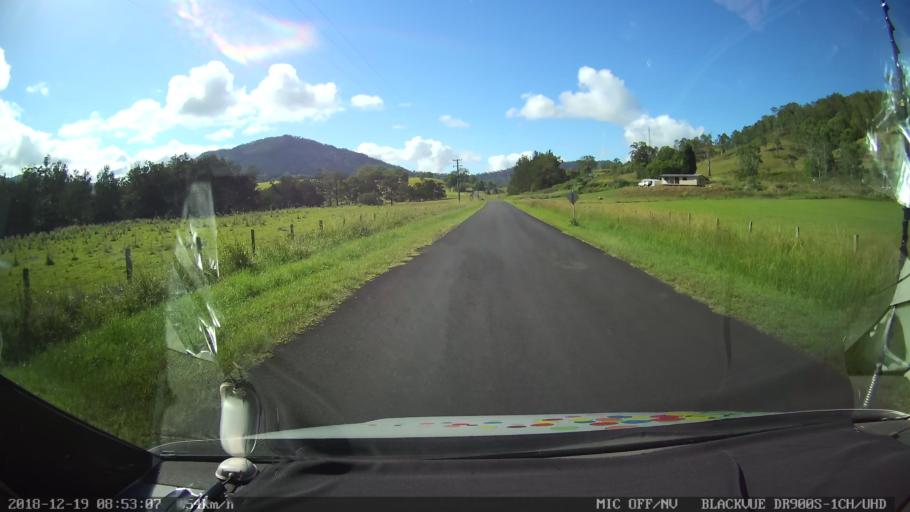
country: AU
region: New South Wales
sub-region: Kyogle
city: Kyogle
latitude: -28.3981
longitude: 152.9769
